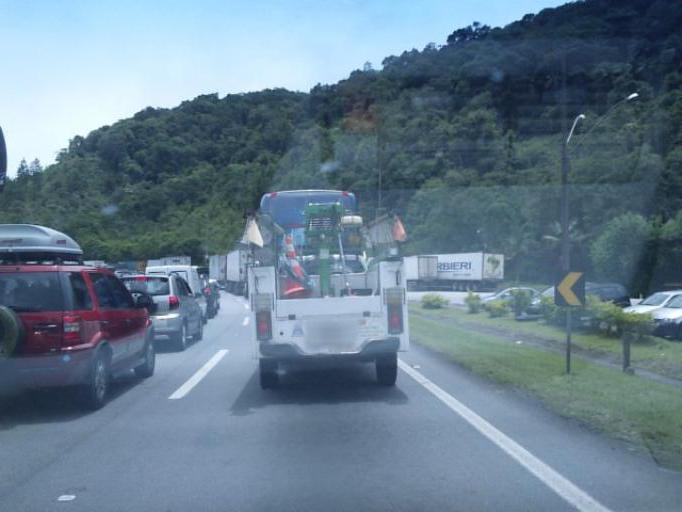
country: BR
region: Sao Paulo
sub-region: Juquitiba
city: Juquitiba
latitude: -24.0508
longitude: -47.2085
